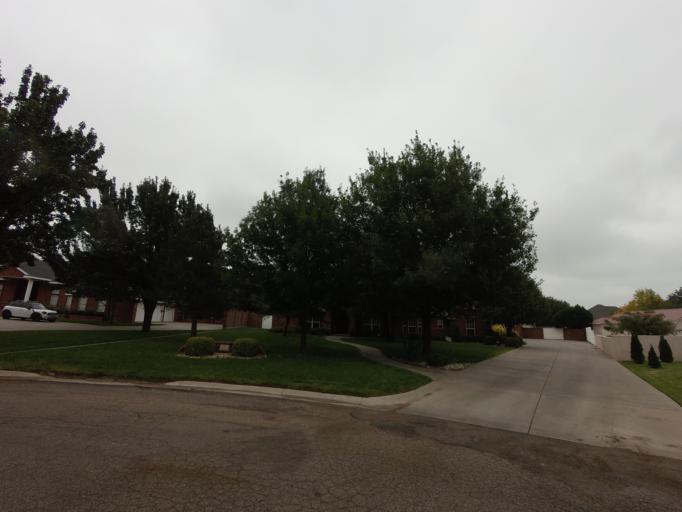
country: US
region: New Mexico
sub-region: Curry County
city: Clovis
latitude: 34.4308
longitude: -103.1834
